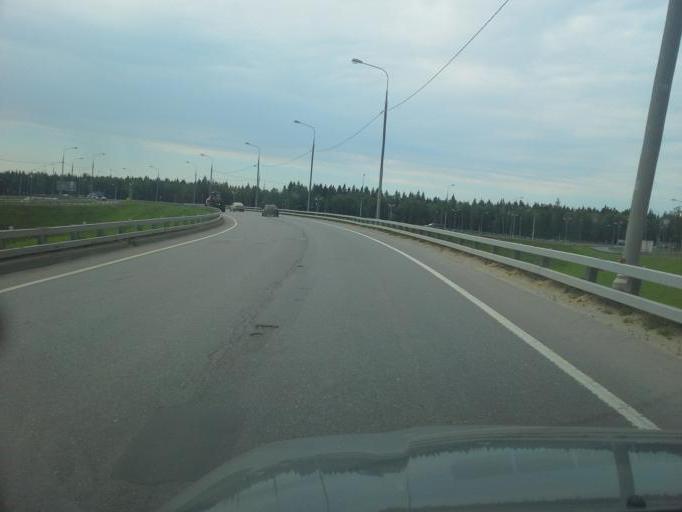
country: RU
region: Moskovskaya
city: Kokoshkino
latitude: 55.5595
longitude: 37.1501
